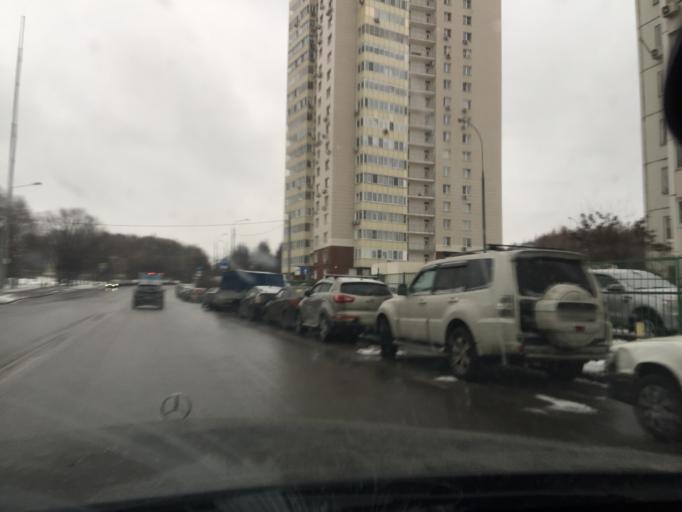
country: RU
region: Moscow
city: Troparevo
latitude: 55.6482
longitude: 37.4693
